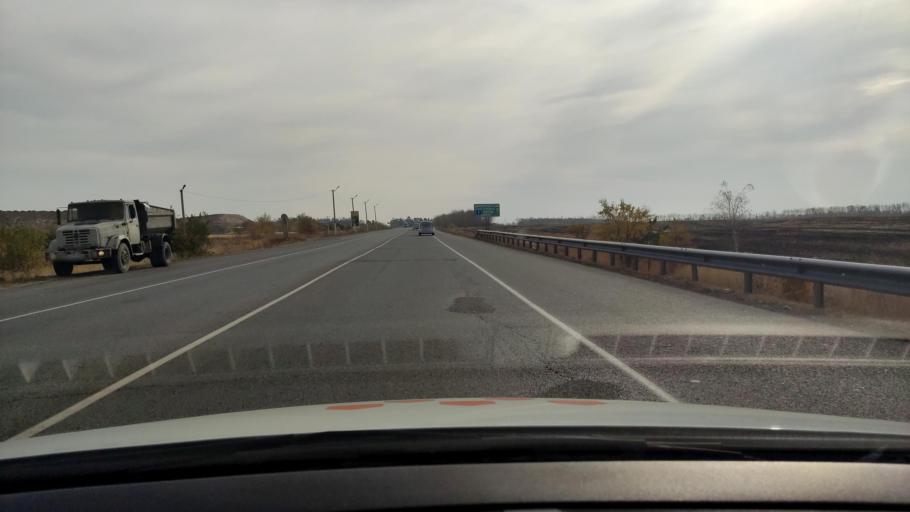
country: RU
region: Voronezj
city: Novaya Usman'
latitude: 51.6876
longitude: 39.4696
